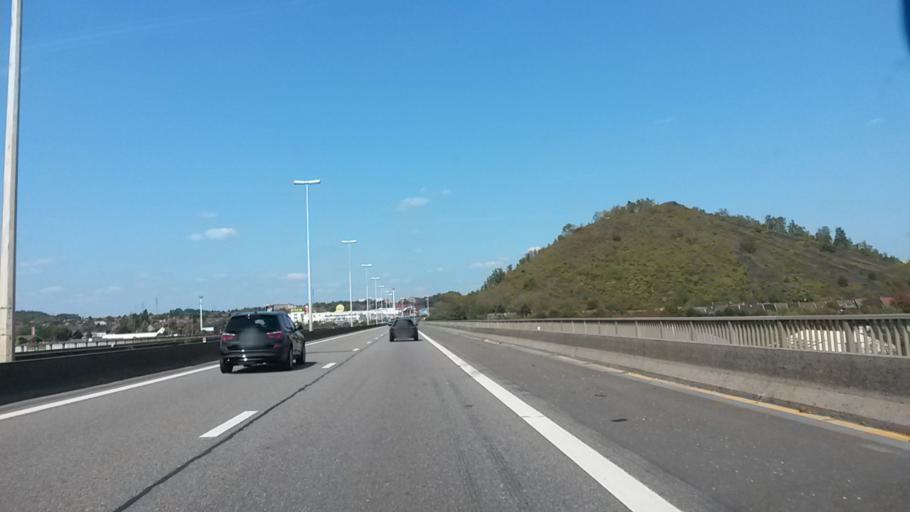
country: BE
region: Wallonia
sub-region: Province du Hainaut
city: Chatelet
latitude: 50.4038
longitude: 4.5030
